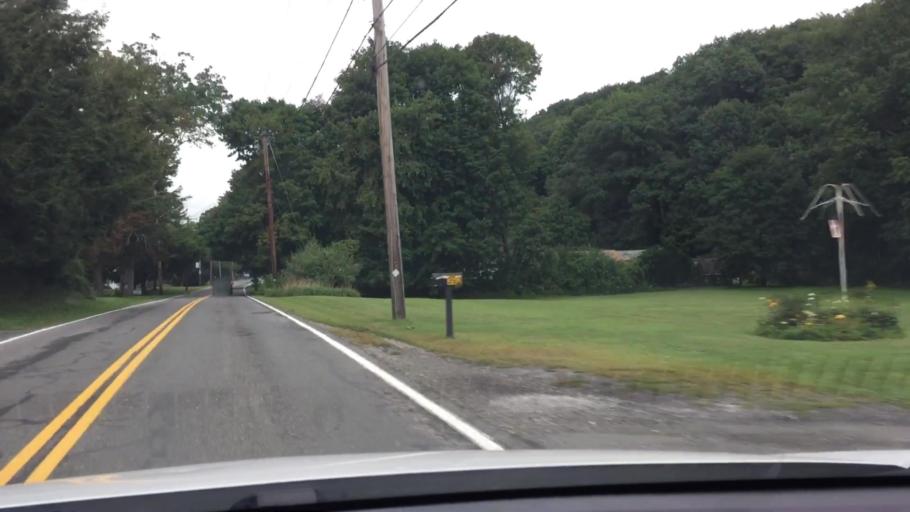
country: US
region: Massachusetts
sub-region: Berkshire County
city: Housatonic
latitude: 42.2535
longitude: -73.3754
